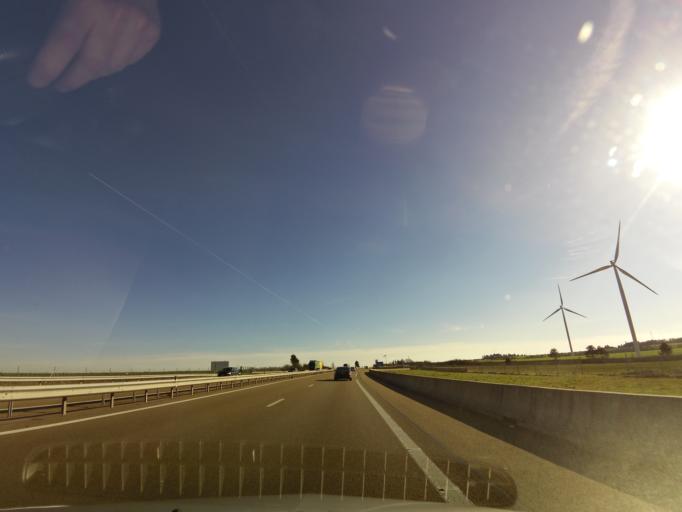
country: FR
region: Bourgogne
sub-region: Departement de l'Yonne
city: Saint-Bris-le-Vineux
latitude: 47.7695
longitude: 3.7251
